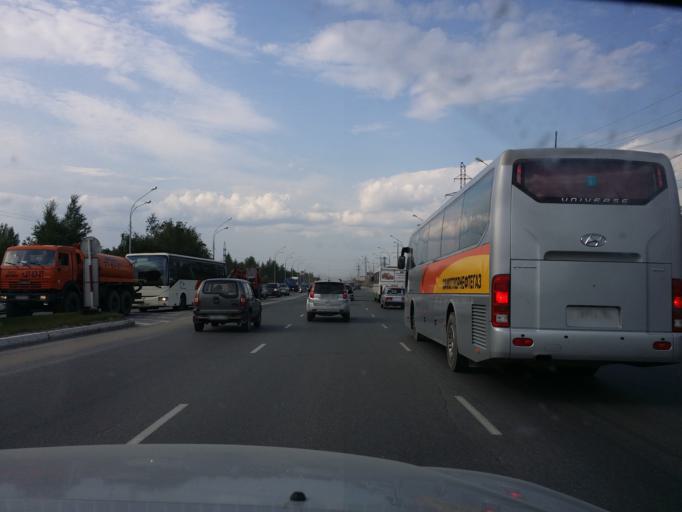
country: RU
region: Khanty-Mansiyskiy Avtonomnyy Okrug
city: Nizhnevartovsk
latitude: 60.9489
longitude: 76.5298
